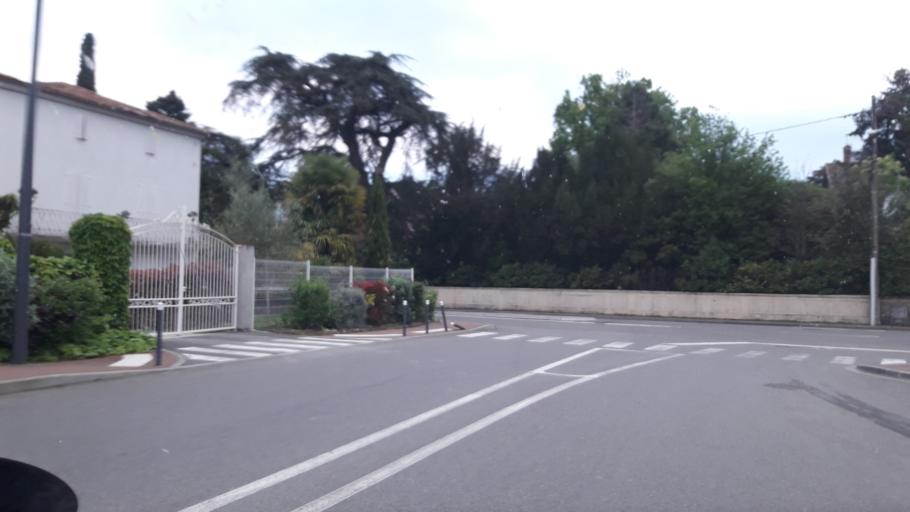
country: FR
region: Midi-Pyrenees
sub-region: Departement de la Haute-Garonne
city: Cazeres
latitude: 43.2113
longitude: 1.0850
